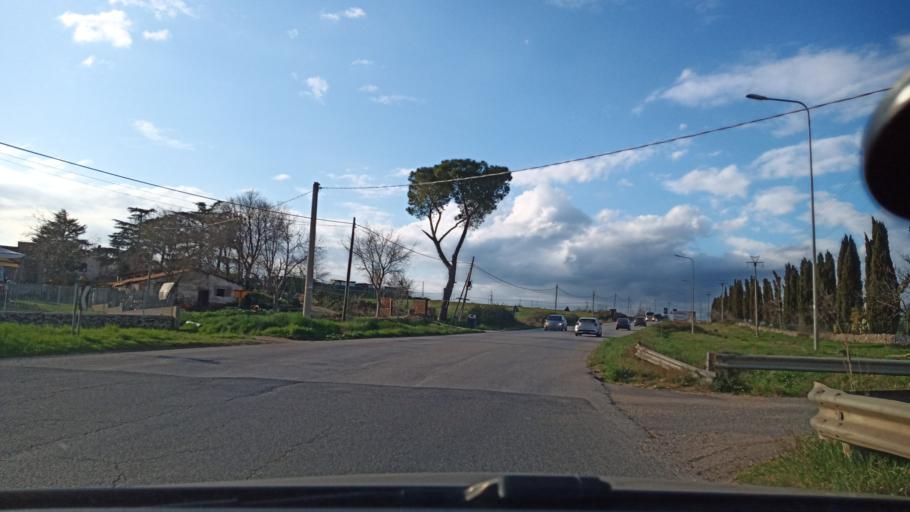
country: IT
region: Latium
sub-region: Citta metropolitana di Roma Capitale
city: Fiano Romano
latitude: 42.1485
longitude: 12.6180
